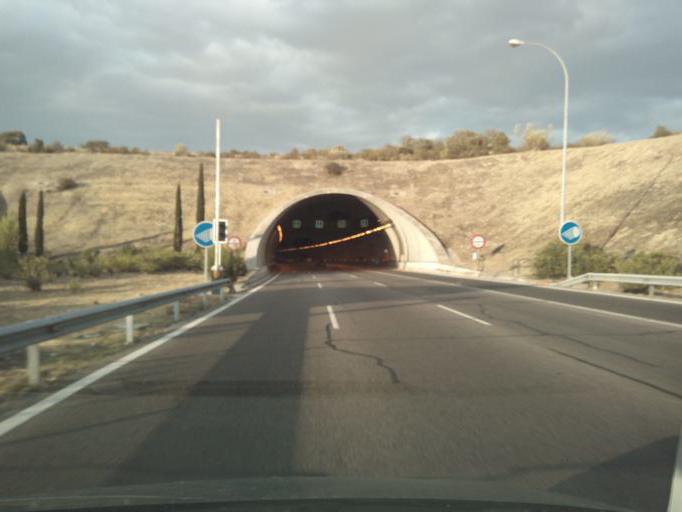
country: ES
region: Madrid
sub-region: Provincia de Madrid
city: Fuencarral-El Pardo
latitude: 40.4801
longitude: -3.7479
